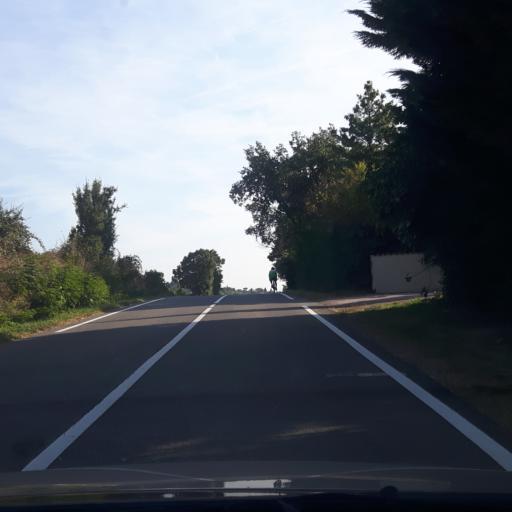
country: FR
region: Midi-Pyrenees
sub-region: Departement de la Haute-Garonne
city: Montjoire
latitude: 43.7601
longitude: 1.5226
